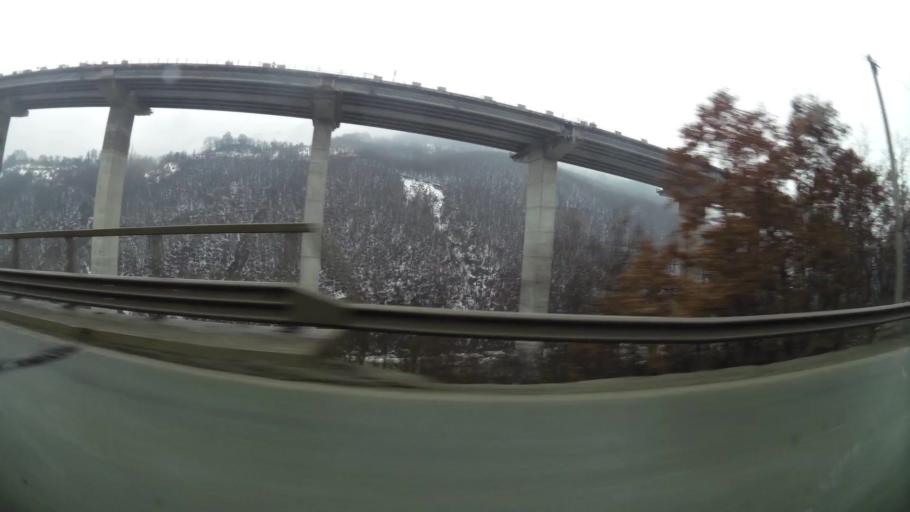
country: XK
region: Ferizaj
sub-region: Hani i Elezit
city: Hani i Elezit
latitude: 42.1726
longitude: 21.2746
